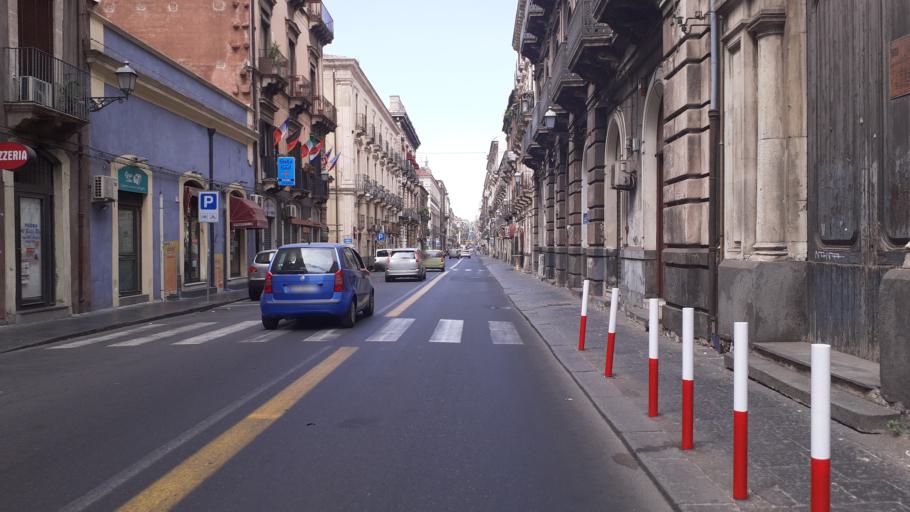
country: IT
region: Sicily
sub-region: Catania
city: Catania
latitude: 37.5033
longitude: 15.0925
